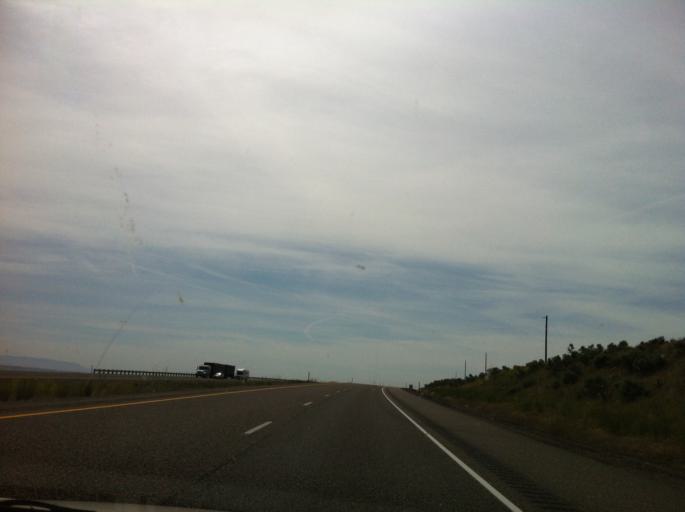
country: US
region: Oregon
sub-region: Malheur County
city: Ontario
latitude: 44.1182
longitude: -117.0658
